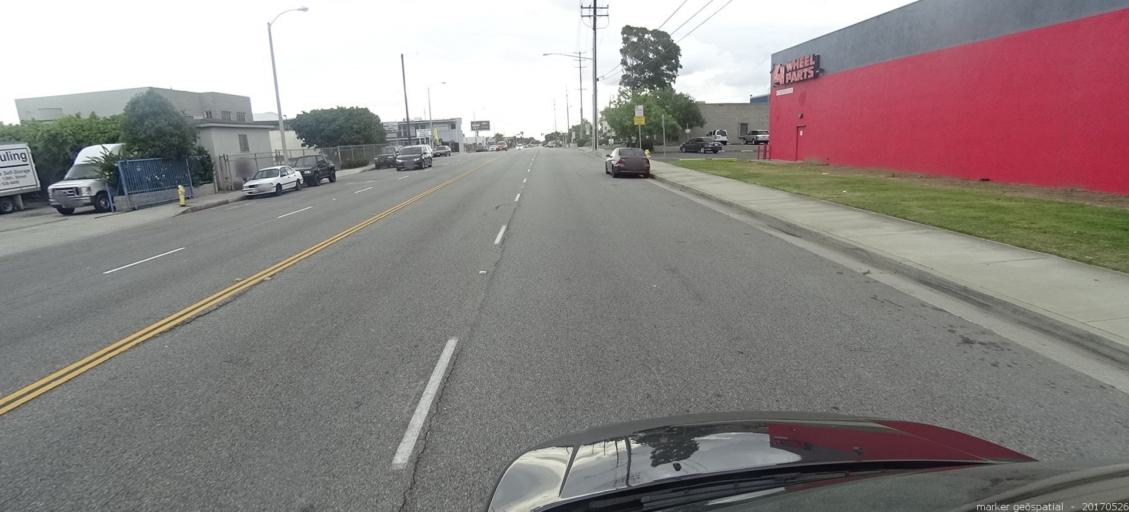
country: US
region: California
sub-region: Los Angeles County
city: Lawndale
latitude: 33.8946
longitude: -118.3644
